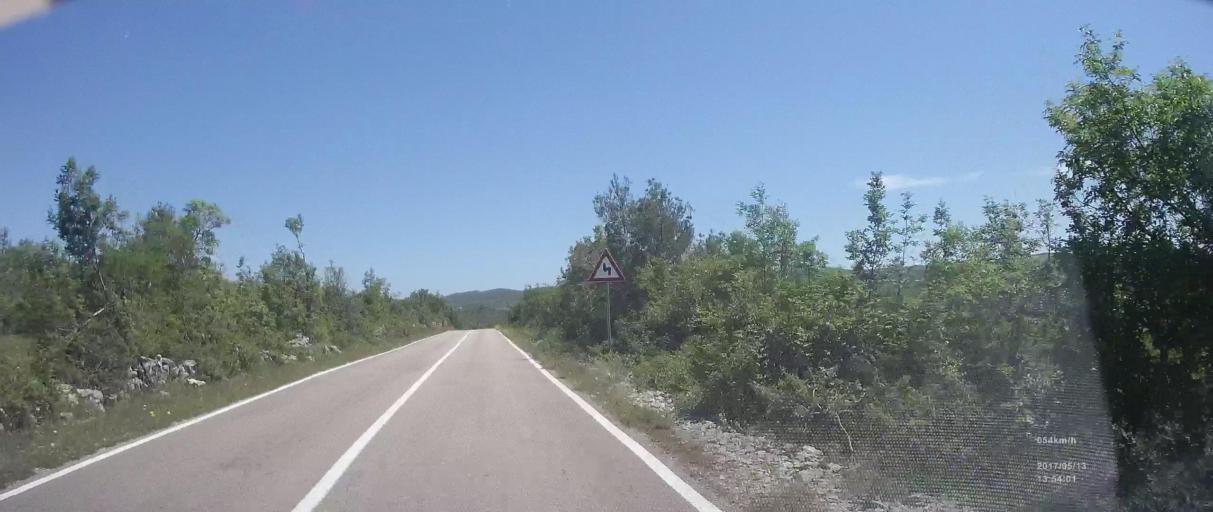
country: HR
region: Sibensko-Kniniska
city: Rogoznica
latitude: 43.5966
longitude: 16.0034
